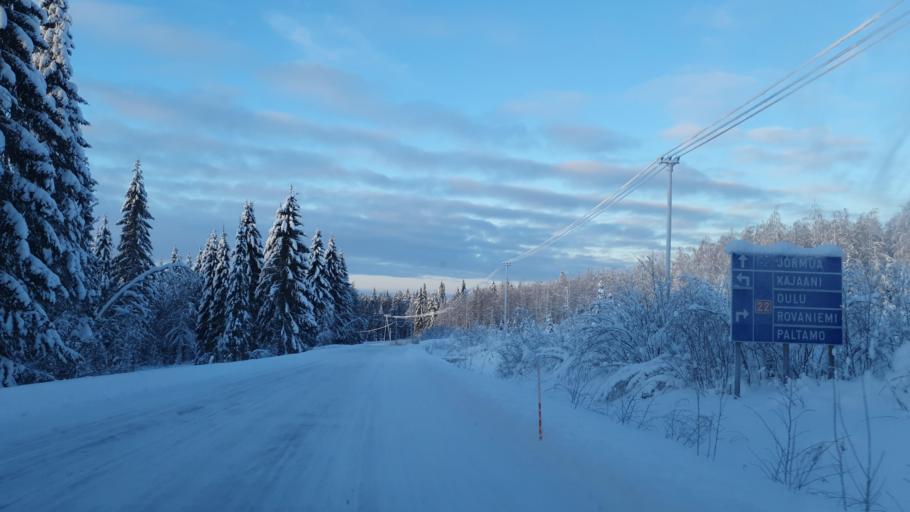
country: FI
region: Kainuu
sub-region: Kajaani
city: Ristijaervi
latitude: 64.3385
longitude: 28.0599
